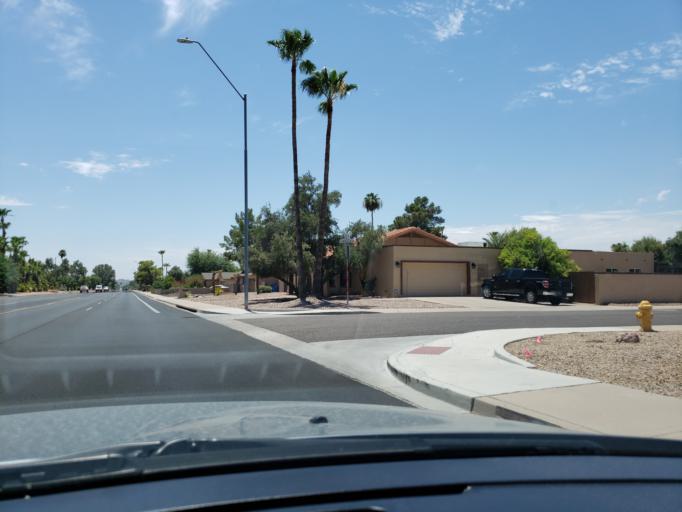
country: US
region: Arizona
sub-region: Maricopa County
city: Paradise Valley
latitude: 33.6157
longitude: -111.9432
